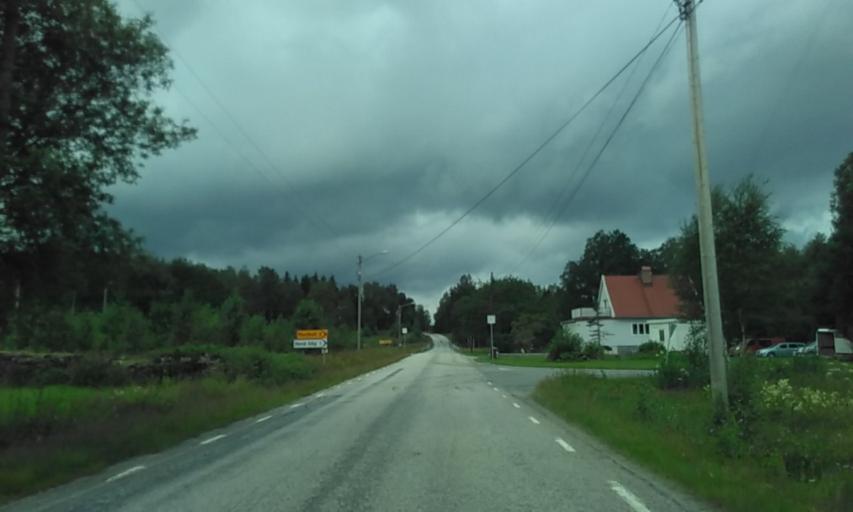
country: SE
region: Vaestra Goetaland
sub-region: Bollebygds Kommun
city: Bollebygd
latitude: 57.7506
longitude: 12.6140
